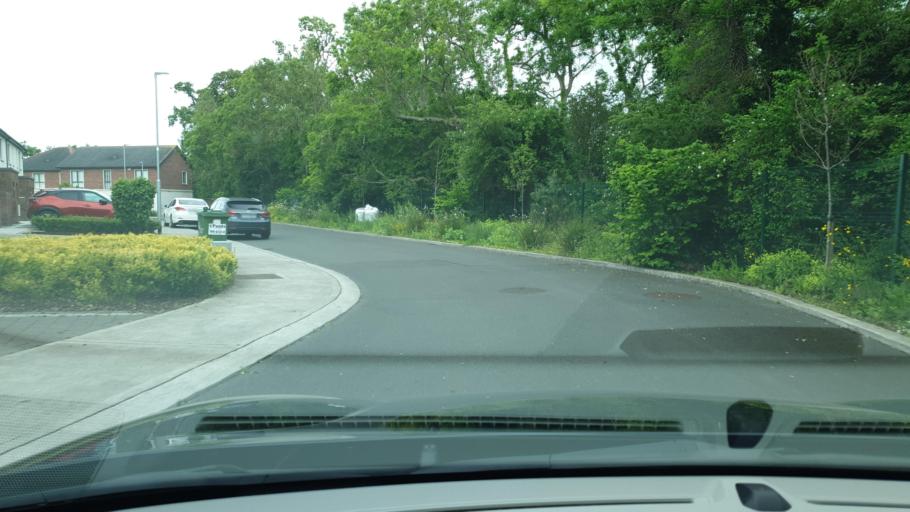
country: IE
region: Leinster
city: Lucan
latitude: 53.3427
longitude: -6.4568
